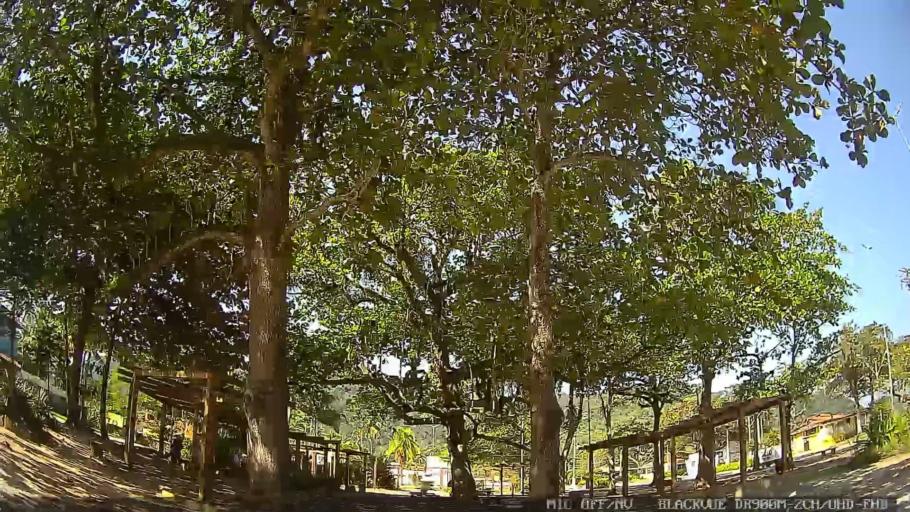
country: BR
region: Sao Paulo
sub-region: Guaruja
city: Guaruja
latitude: -24.0189
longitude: -46.2963
